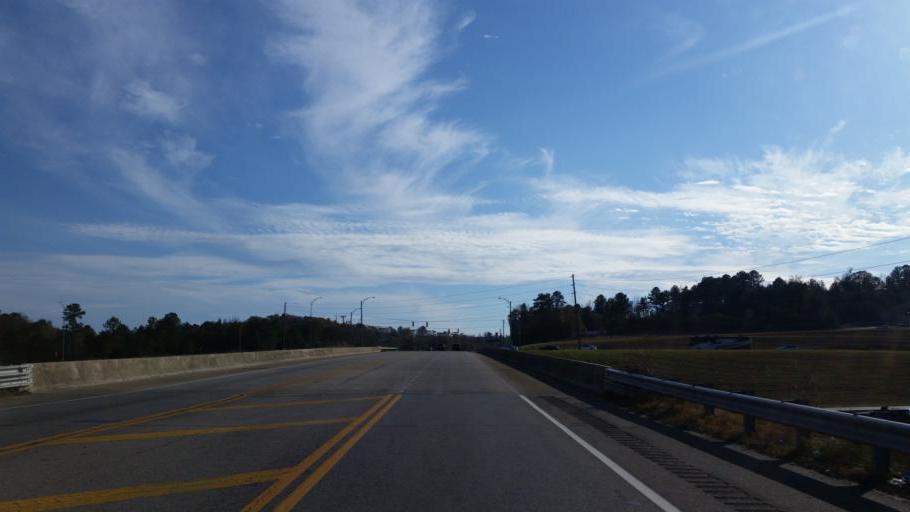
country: US
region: Alabama
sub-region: Tuscaloosa County
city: Holt
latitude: 33.1735
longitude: -87.4476
